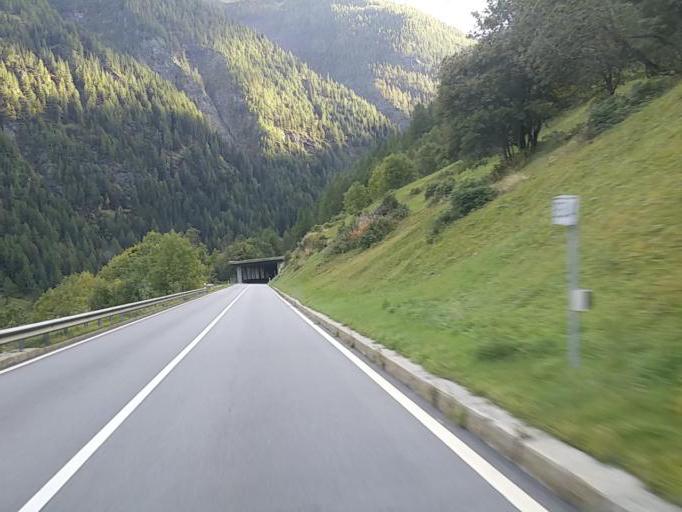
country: IT
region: Piedmont
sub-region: Provincia Verbano-Cusio-Ossola
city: Antronapiana
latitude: 46.1838
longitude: 8.0698
